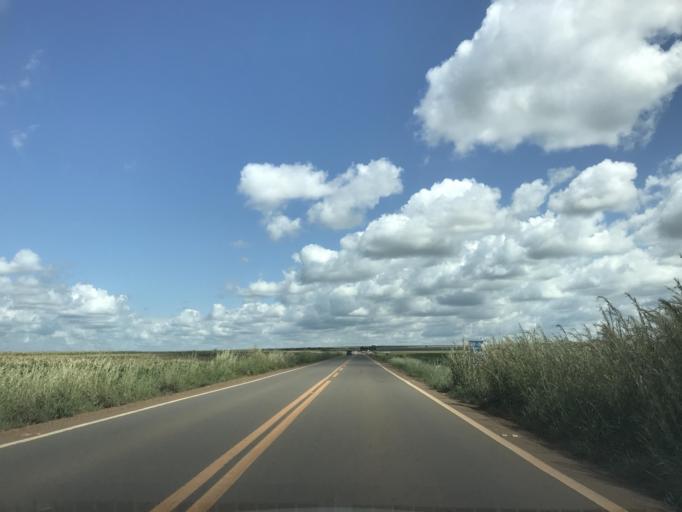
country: BR
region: Goias
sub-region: Luziania
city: Luziania
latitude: -16.4964
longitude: -48.2033
